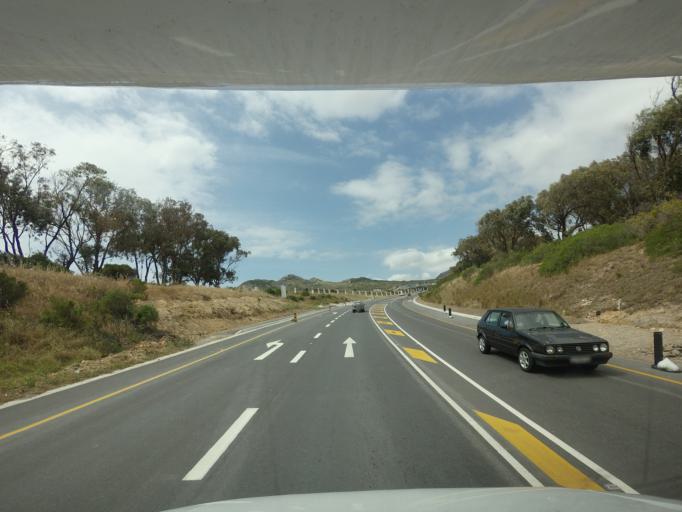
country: ZA
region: Western Cape
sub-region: City of Cape Town
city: Bergvliet
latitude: -34.1311
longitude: 18.3960
